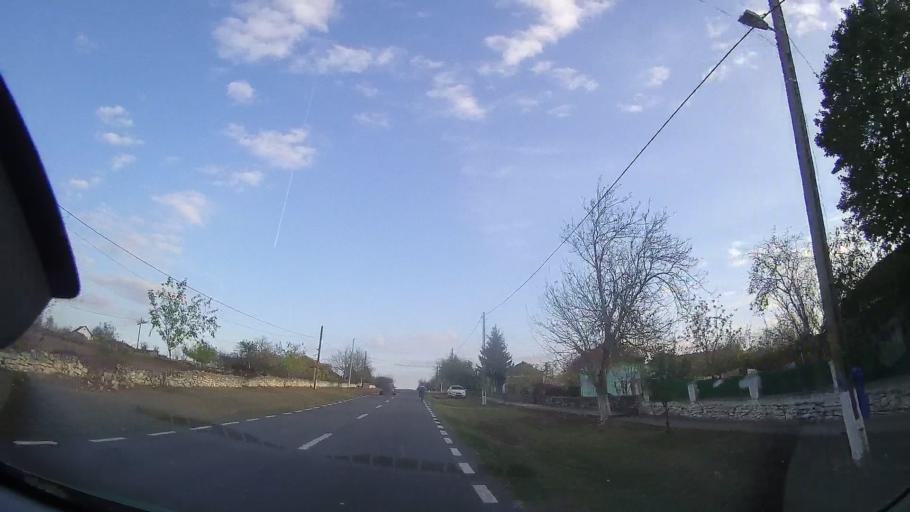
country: RO
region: Constanta
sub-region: Comuna Chirnogeni
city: Plopeni
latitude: 43.9598
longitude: 28.1447
